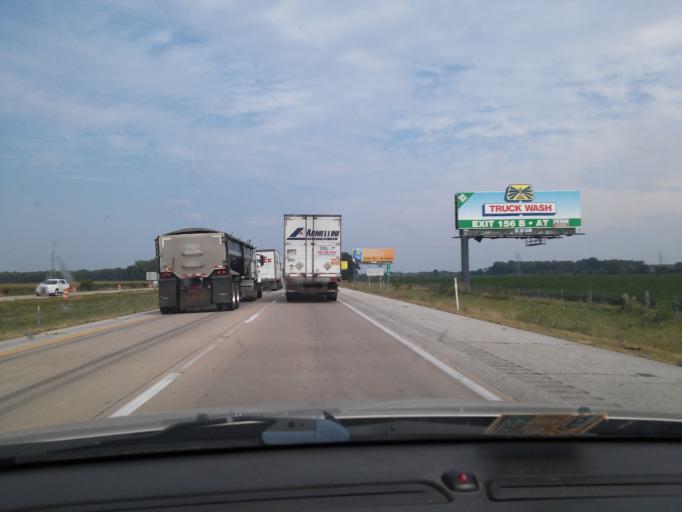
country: US
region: Indiana
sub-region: Wayne County
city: Centerville
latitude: 39.8595
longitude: -84.9830
